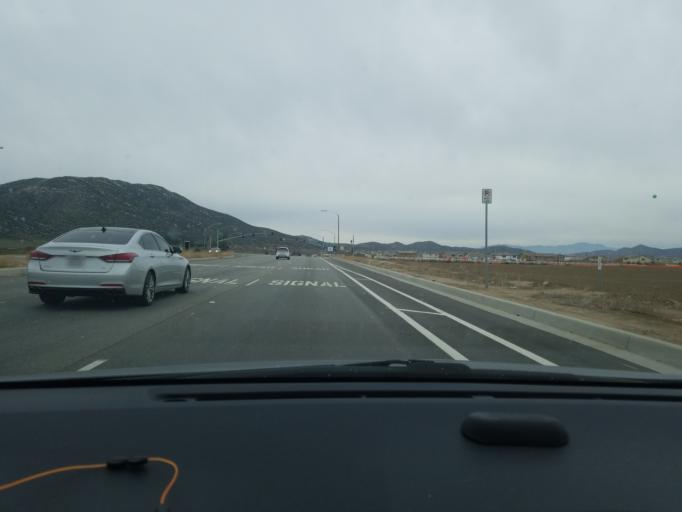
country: US
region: California
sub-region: Riverside County
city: Winchester
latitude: 33.6952
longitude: -117.0908
